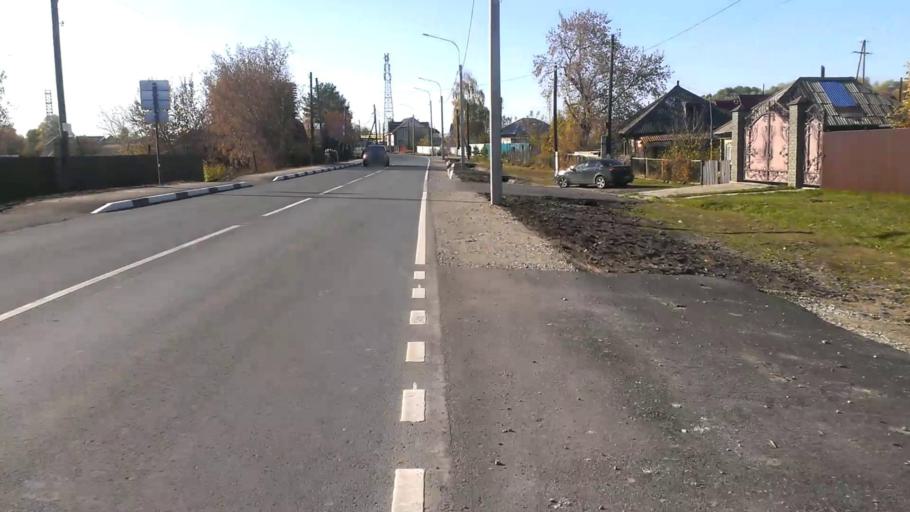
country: RU
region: Altai Krai
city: Sannikovo
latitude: 53.3174
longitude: 83.9503
